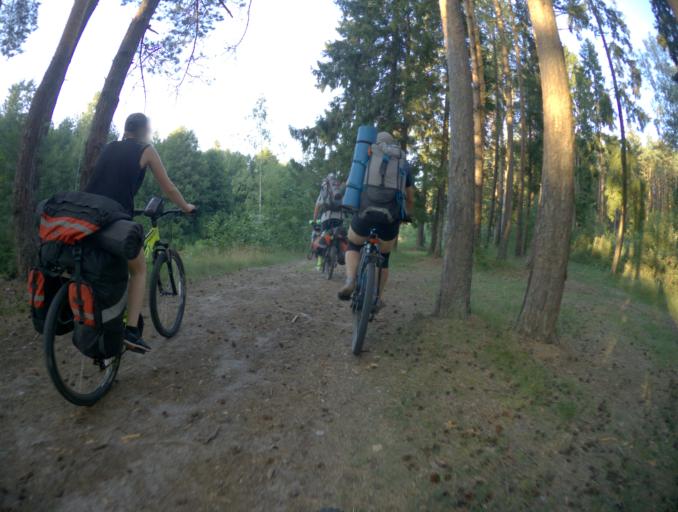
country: RU
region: Nizjnij Novgorod
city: Sitniki
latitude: 56.4672
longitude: 44.0144
